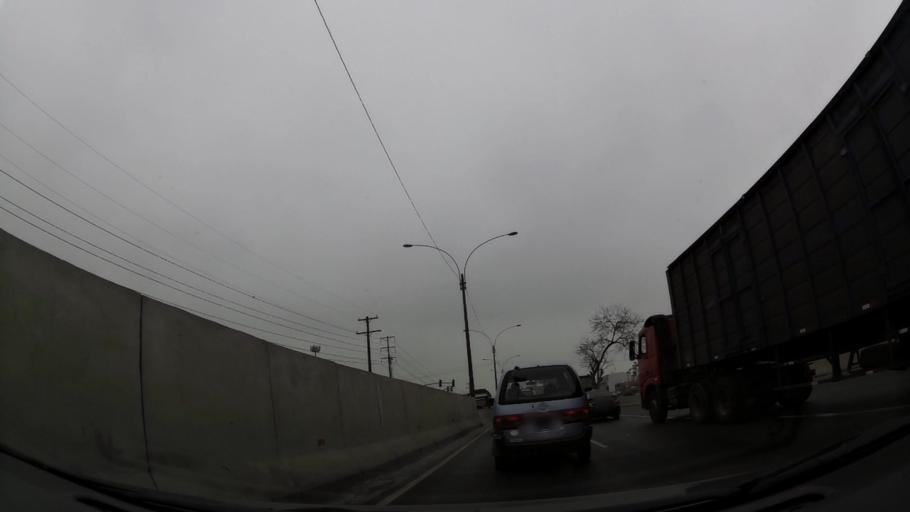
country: PE
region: Lima
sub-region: Lima
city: Urb. Santo Domingo
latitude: -11.9243
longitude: -77.0731
